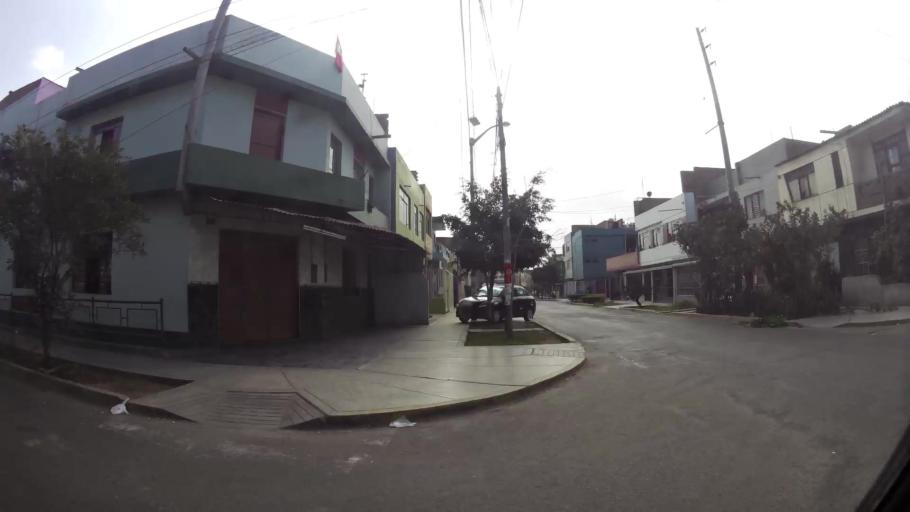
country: PE
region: La Libertad
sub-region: Provincia de Trujillo
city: Trujillo
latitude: -8.1089
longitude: -79.0128
